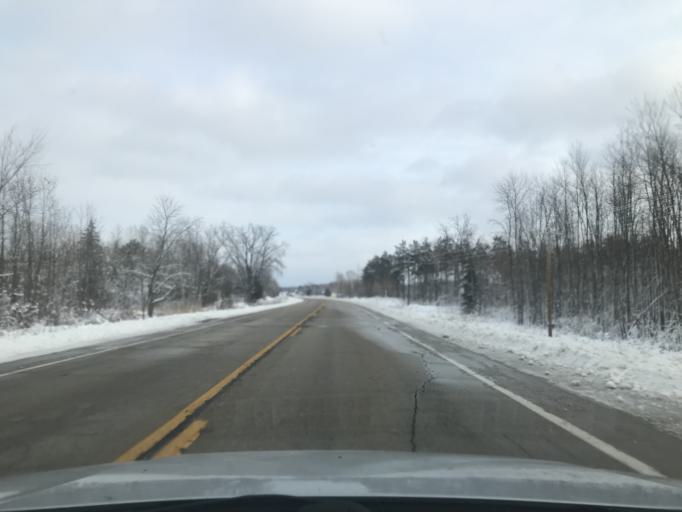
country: US
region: Wisconsin
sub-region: Oconto County
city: Oconto Falls
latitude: 44.8867
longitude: -88.0366
